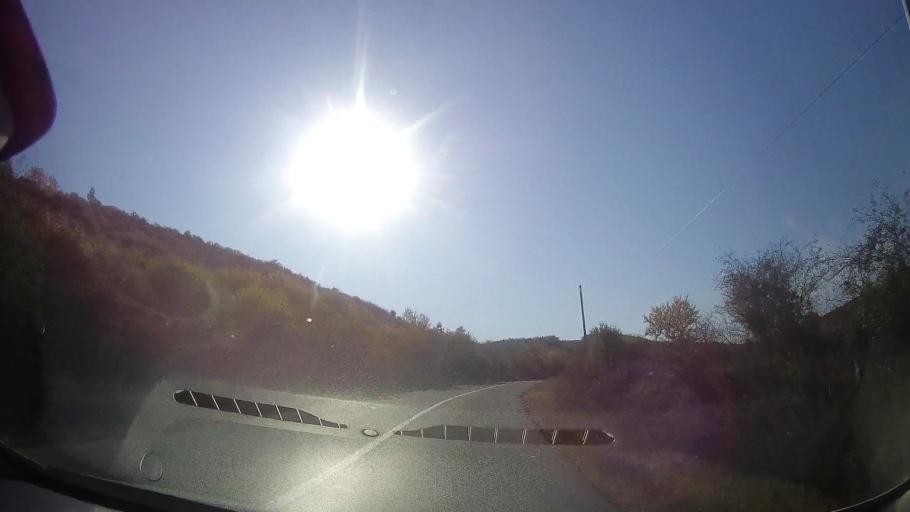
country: RO
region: Timis
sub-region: Oras Recas
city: Recas
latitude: 45.8411
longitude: 21.5215
